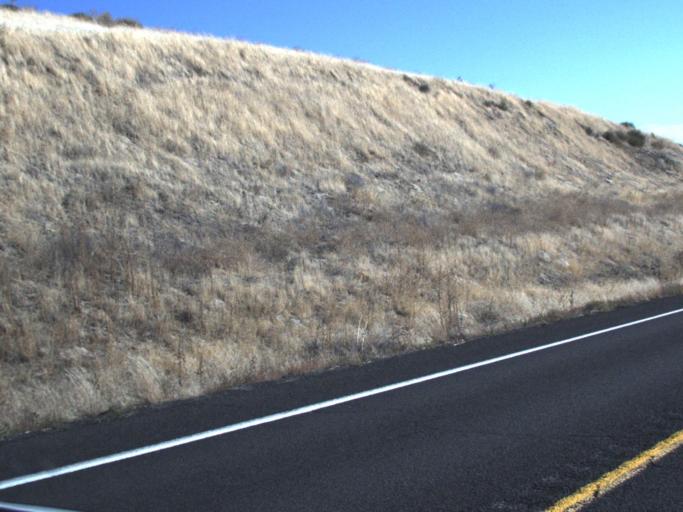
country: US
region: Washington
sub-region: Walla Walla County
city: Garrett
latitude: 46.2896
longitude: -118.5551
